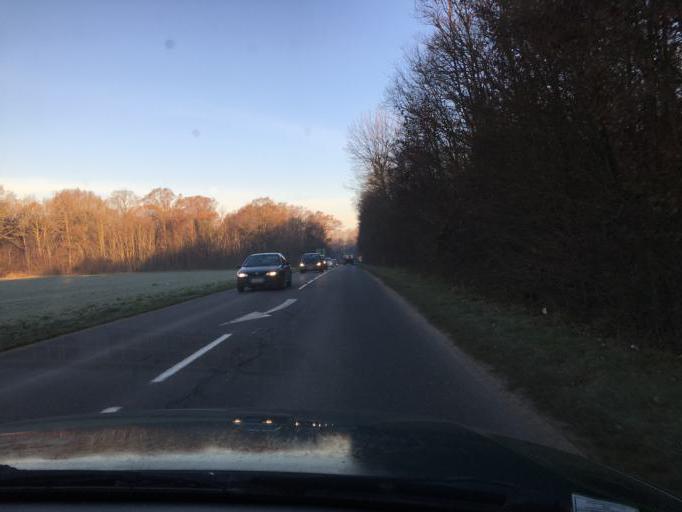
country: FR
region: Centre
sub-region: Departement du Loiret
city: Saran
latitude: 47.9652
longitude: 1.8691
